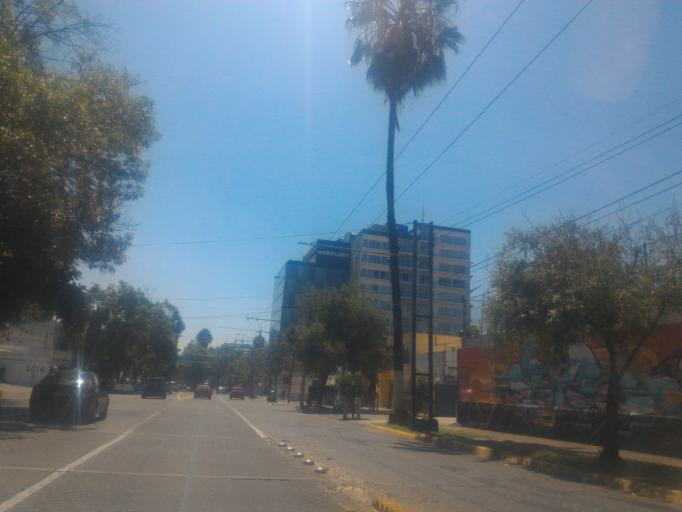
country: MX
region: Jalisco
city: Guadalajara
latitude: 20.6767
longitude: -103.3824
